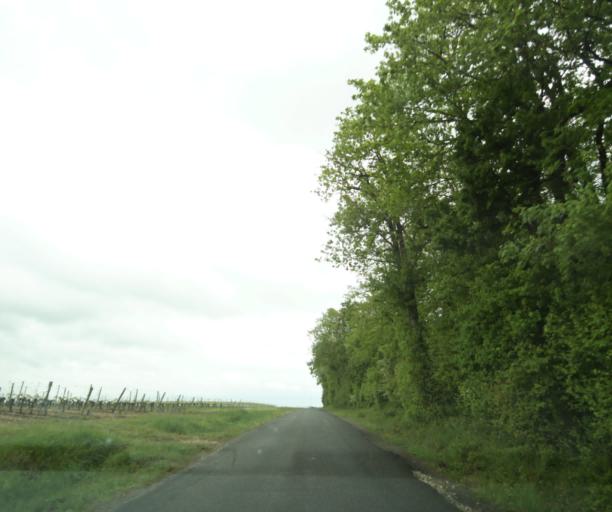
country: FR
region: Poitou-Charentes
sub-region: Departement de la Charente-Maritime
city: Perignac
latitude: 45.6736
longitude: -0.4959
